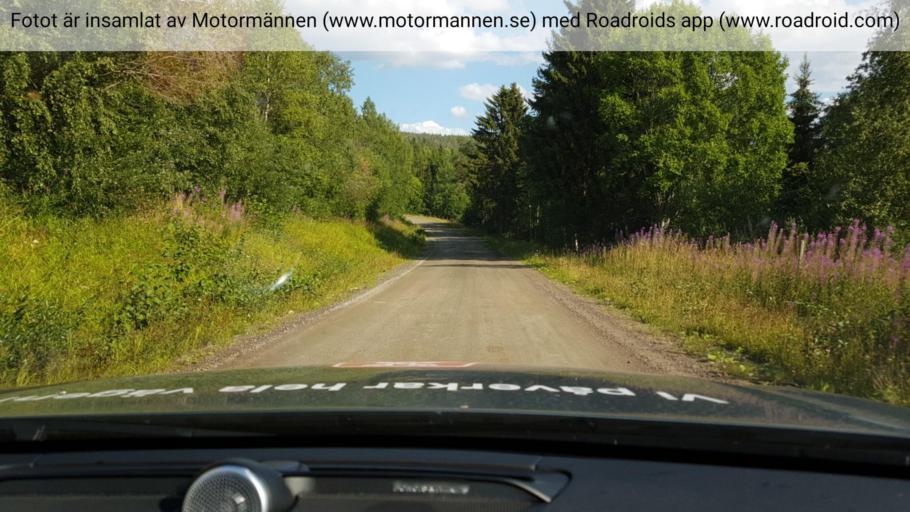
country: SE
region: Jaemtland
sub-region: Stroemsunds Kommun
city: Stroemsund
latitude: 63.9910
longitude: 15.9971
